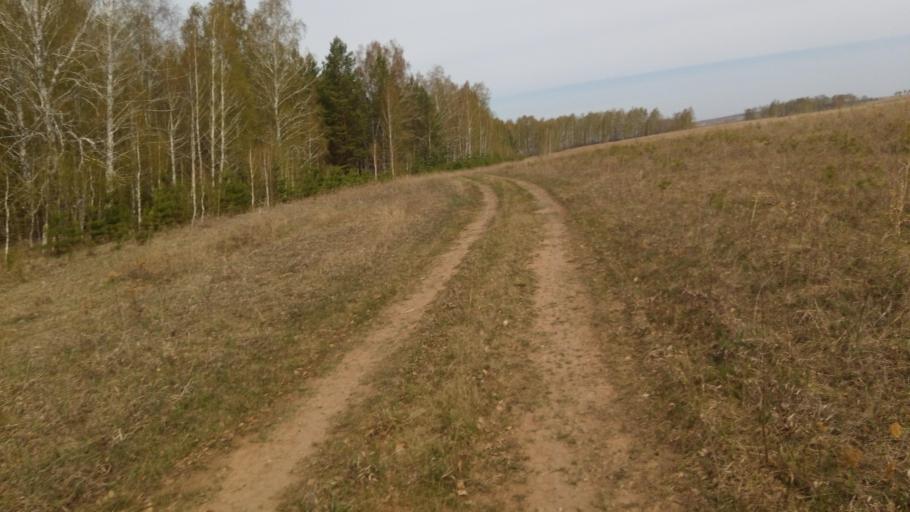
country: RU
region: Chelyabinsk
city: Timiryazevskiy
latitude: 55.0191
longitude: 60.8599
